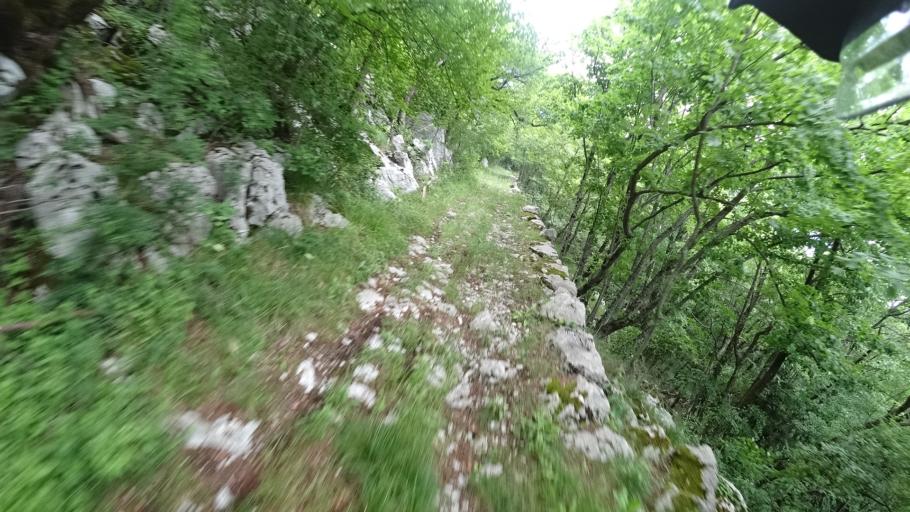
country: HR
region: Primorsko-Goranska
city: Bribir
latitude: 45.2228
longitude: 14.7471
